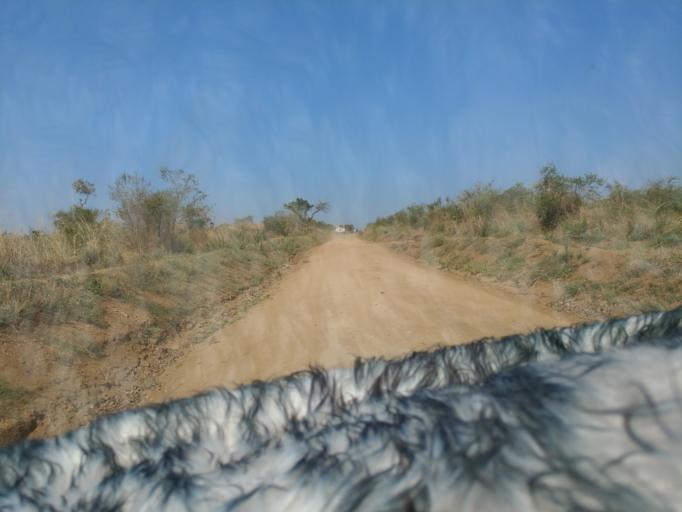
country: UG
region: Northern Region
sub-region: Yumbe District
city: Yumbe
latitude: 3.3916
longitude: 31.3483
